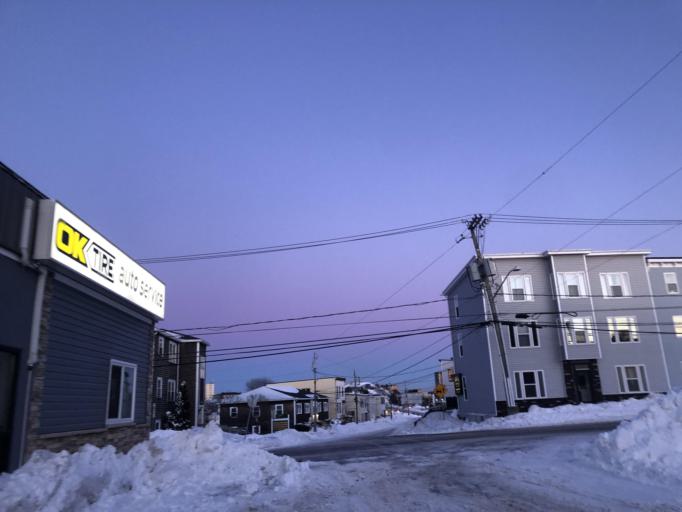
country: CA
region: New Brunswick
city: Saint John
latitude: 45.2762
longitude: -66.0808
